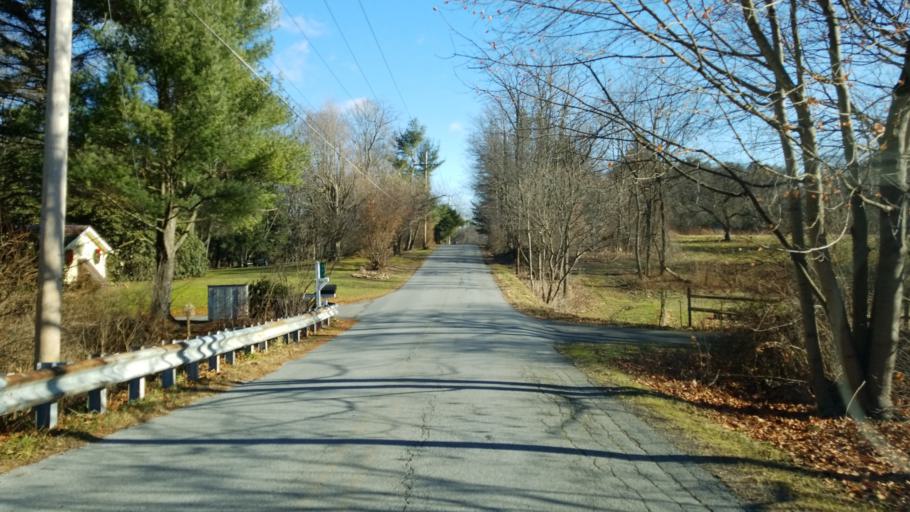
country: US
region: Pennsylvania
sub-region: Clearfield County
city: Hyde
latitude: 40.9828
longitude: -78.4875
